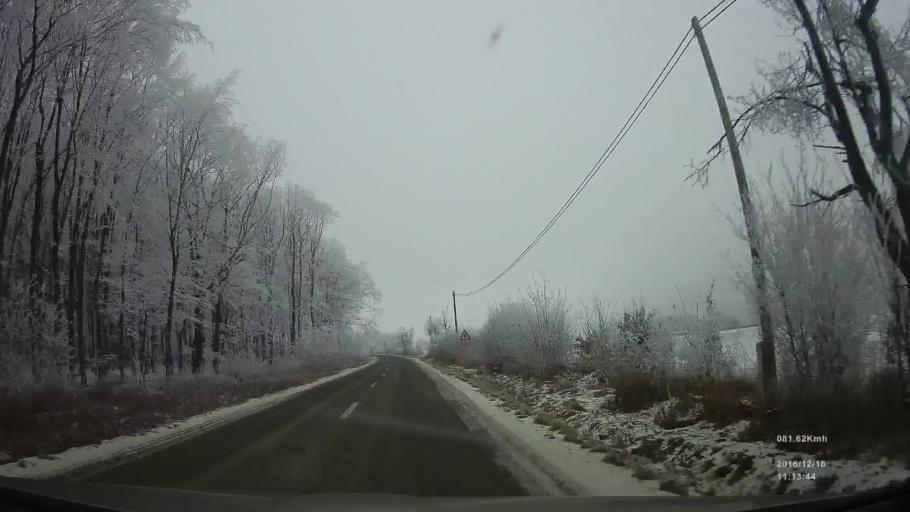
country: SK
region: Presovsky
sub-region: Okres Presov
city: Presov
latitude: 48.8856
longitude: 21.3140
